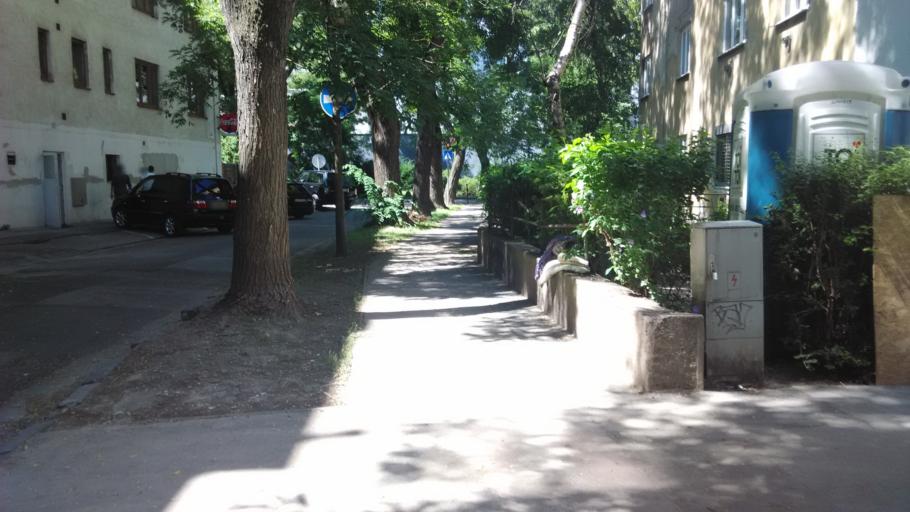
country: SK
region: Bratislavsky
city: Bratislava
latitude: 48.1508
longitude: 17.1247
